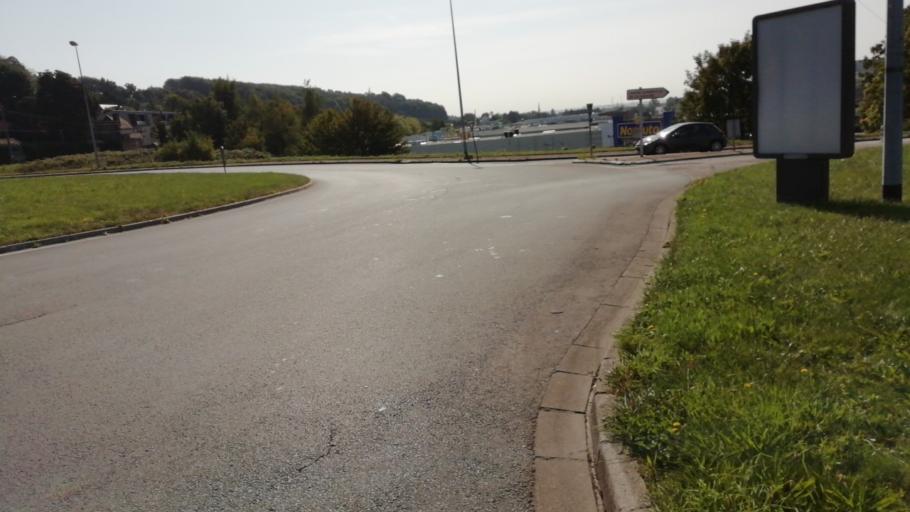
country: FR
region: Haute-Normandie
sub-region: Departement de la Seine-Maritime
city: Montivilliers
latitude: 49.5306
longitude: 0.1892
